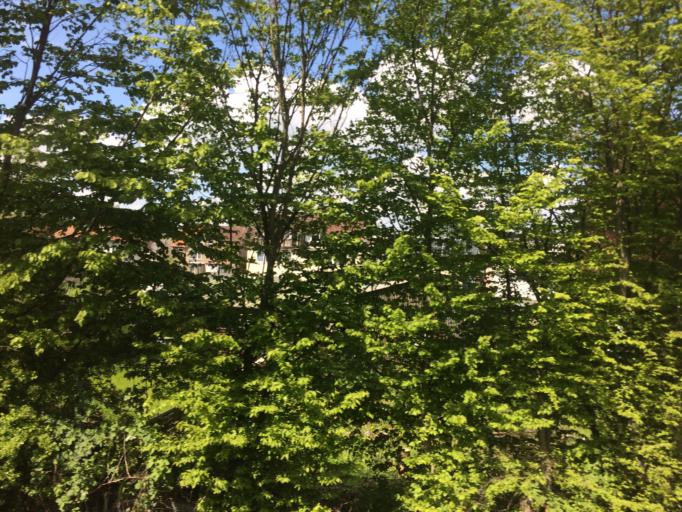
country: DE
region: Schleswig-Holstein
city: Neumunster
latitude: 54.0655
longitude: 9.9707
